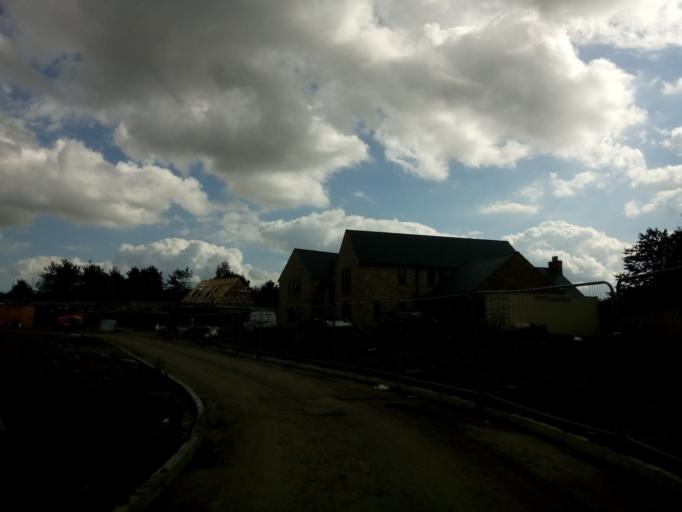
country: GB
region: England
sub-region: County Durham
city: West Rainton
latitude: 54.7909
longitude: -1.5186
